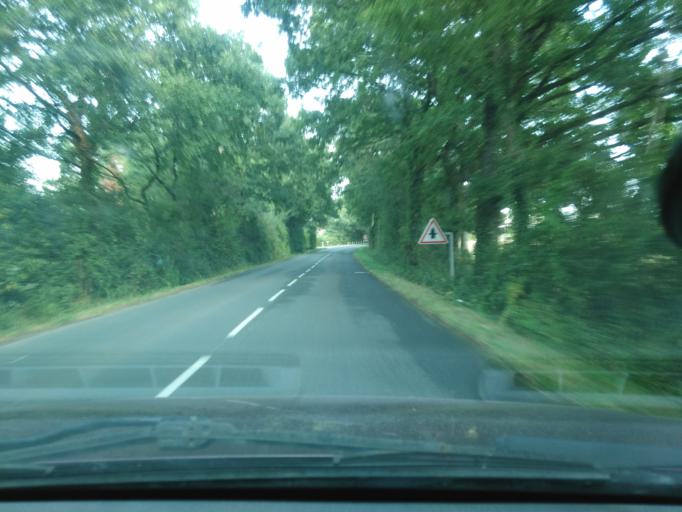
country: FR
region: Pays de la Loire
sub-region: Departement de la Vendee
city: La Roche-sur-Yon
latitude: 46.6418
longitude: -1.4462
